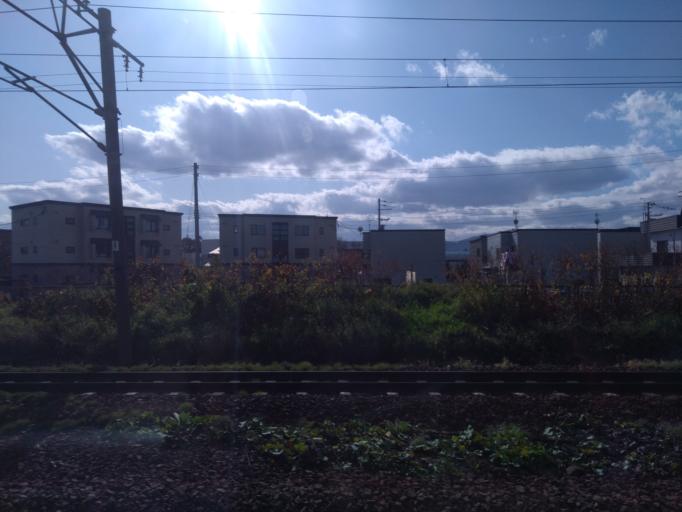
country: JP
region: Hokkaido
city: Sapporo
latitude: 43.0667
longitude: 141.3938
